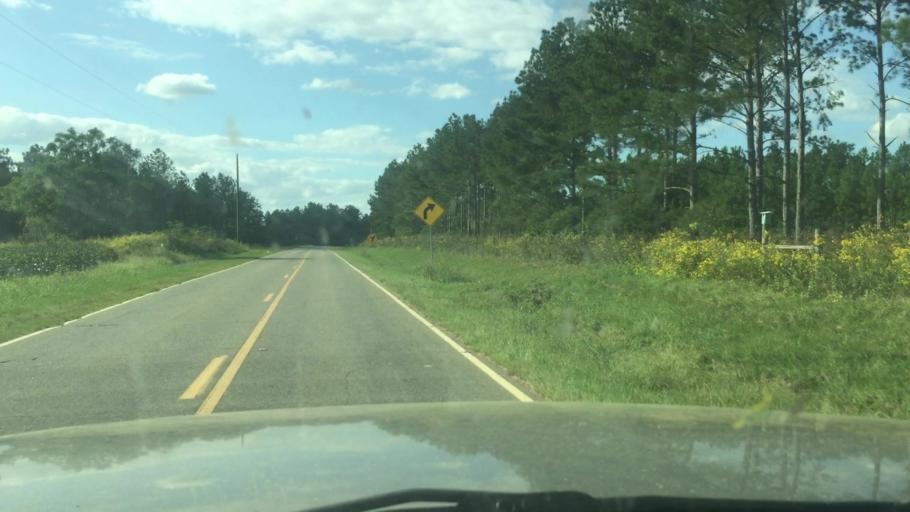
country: US
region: Georgia
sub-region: Terrell County
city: Dawson
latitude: 31.7413
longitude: -84.3484
